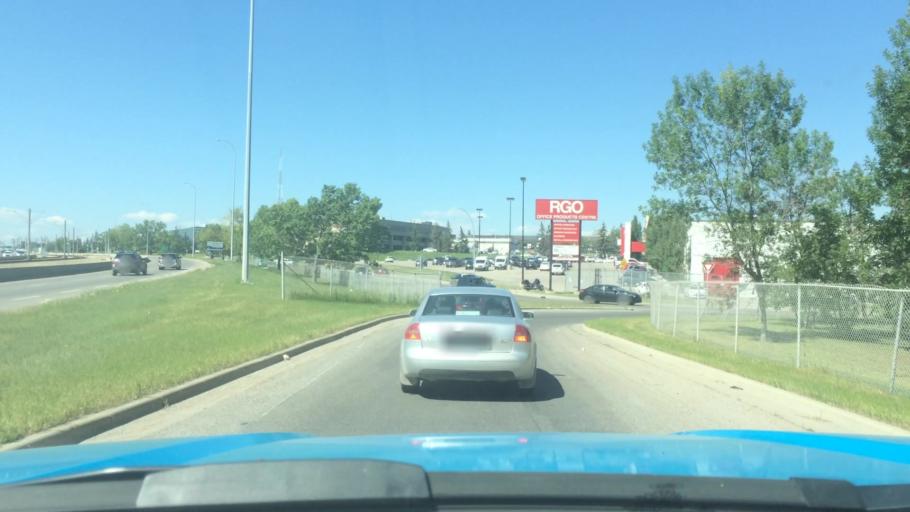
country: CA
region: Alberta
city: Calgary
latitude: 51.0519
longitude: -113.9851
